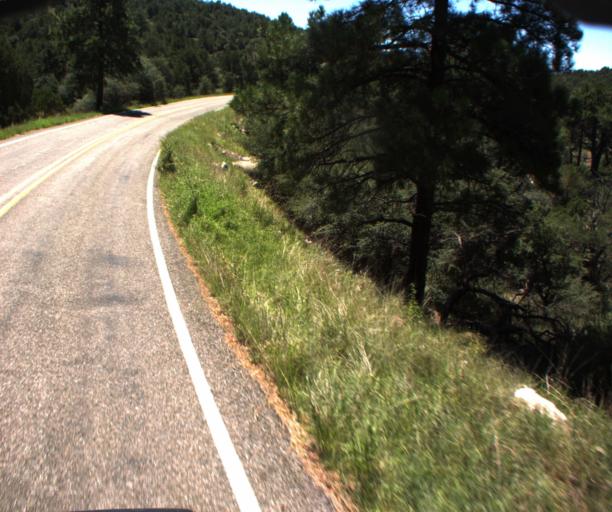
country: US
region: Arizona
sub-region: Greenlee County
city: Morenci
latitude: 33.2835
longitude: -109.3546
